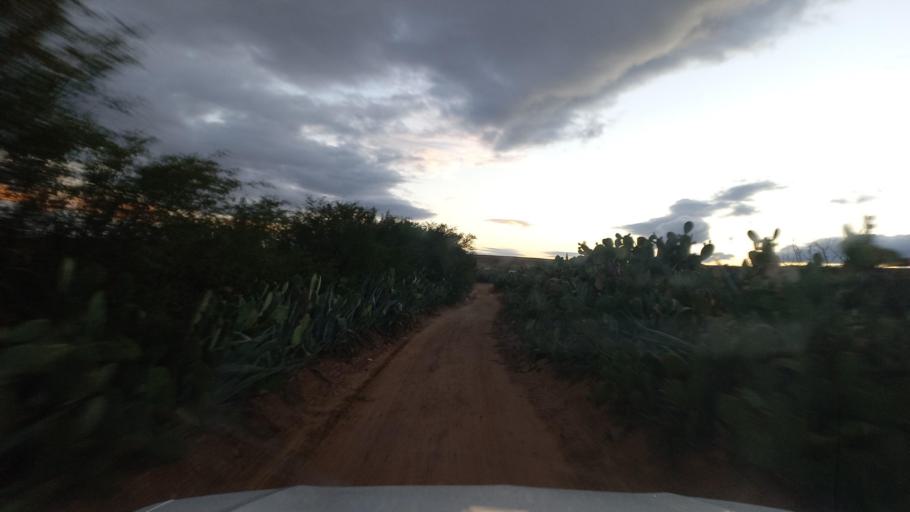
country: TN
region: Al Qasrayn
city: Kasserine
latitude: 35.2548
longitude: 8.9357
